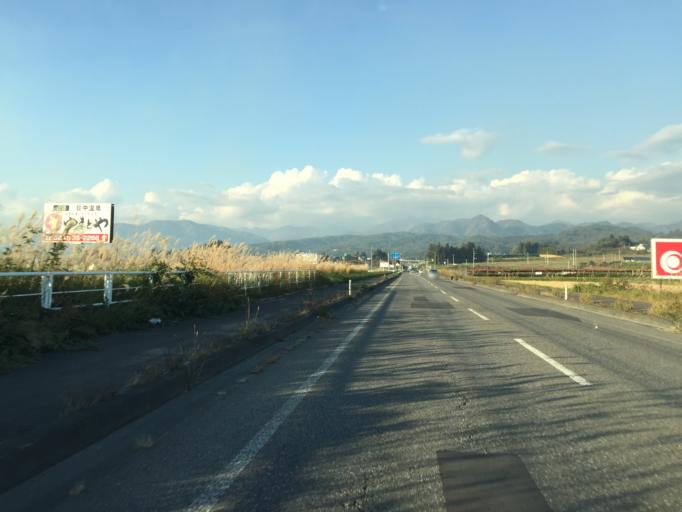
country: JP
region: Fukushima
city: Kitakata
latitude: 37.6799
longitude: 139.8884
